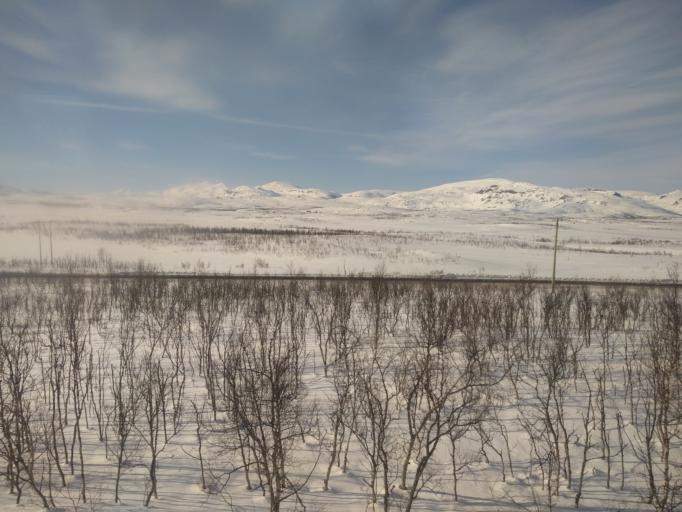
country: NO
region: Troms
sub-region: Bardu
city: Setermoen
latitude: 68.4270
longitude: 18.3950
